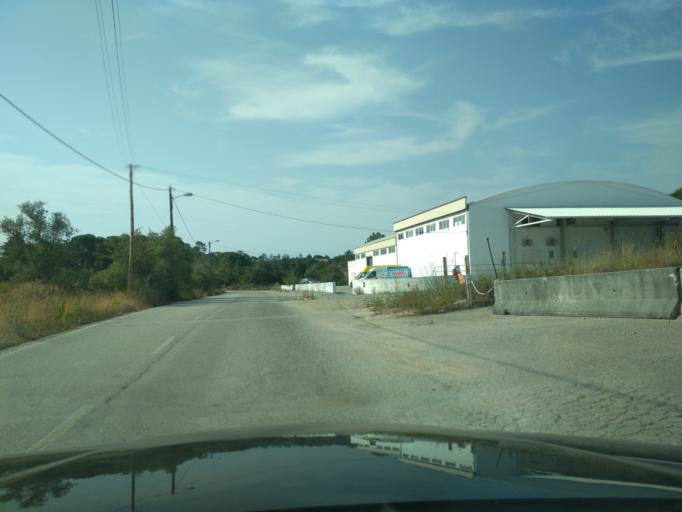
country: PT
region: Coimbra
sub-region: Condeixa-A-Nova
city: Condeixa-a-Nova
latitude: 40.1440
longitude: -8.4591
